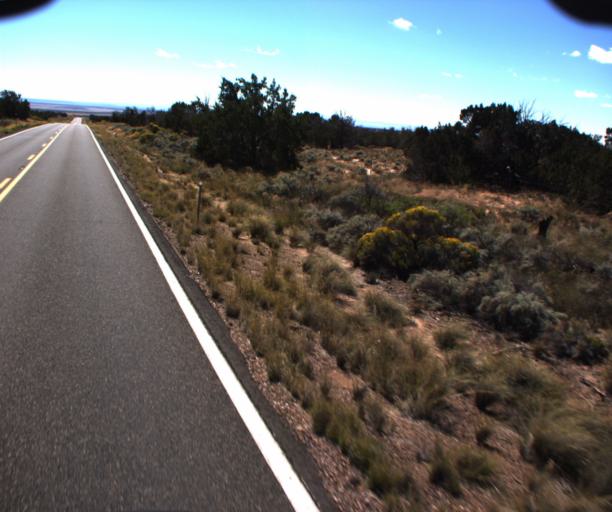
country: US
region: Arizona
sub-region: Apache County
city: Saint Johns
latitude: 34.8305
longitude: -109.2375
